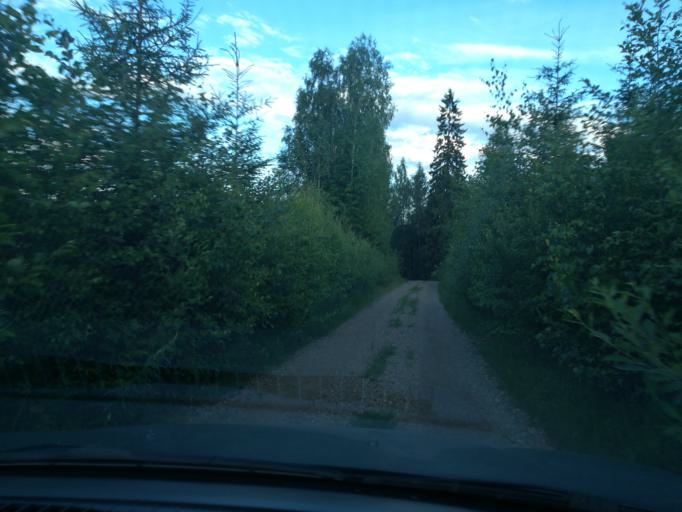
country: FI
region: Southern Savonia
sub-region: Mikkeli
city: Puumala
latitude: 61.6140
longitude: 28.1571
